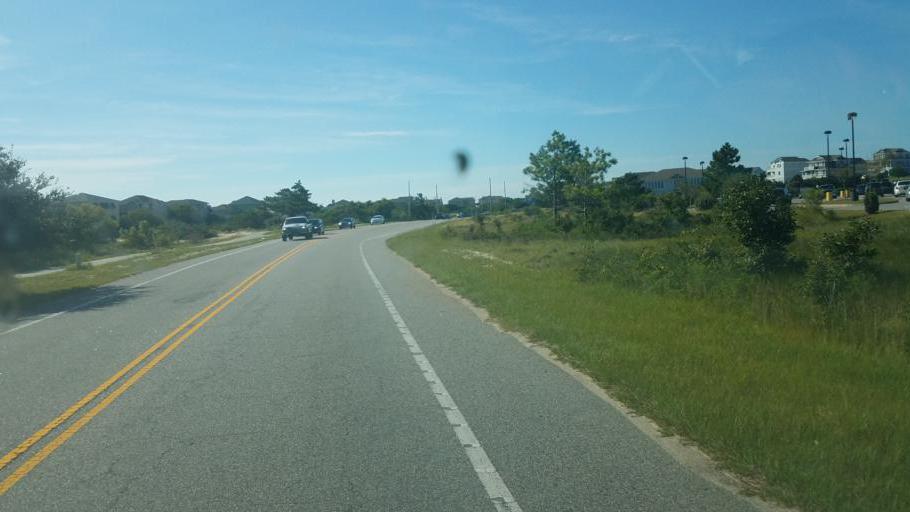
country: US
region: North Carolina
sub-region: Dare County
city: Southern Shores
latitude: 36.3036
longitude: -75.8055
